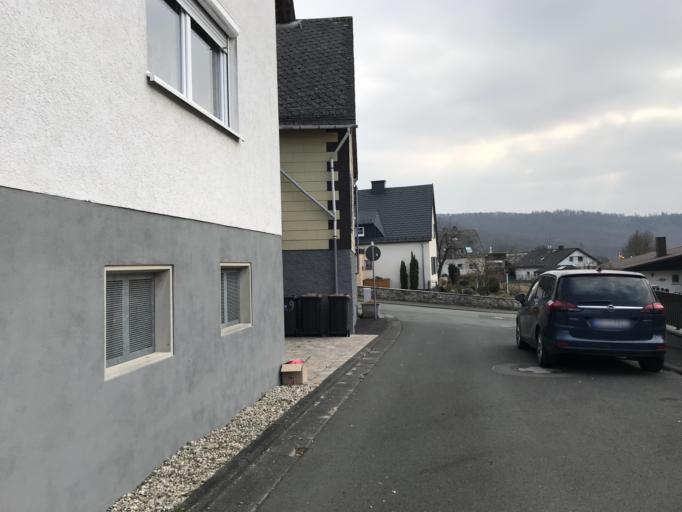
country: DE
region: Hesse
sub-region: Regierungsbezirk Giessen
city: Sinn
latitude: 50.6549
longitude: 8.3336
